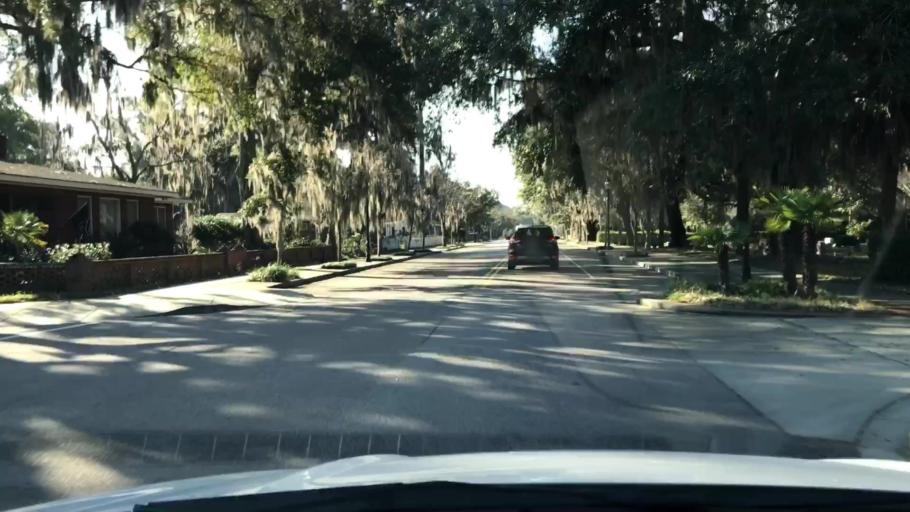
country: US
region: South Carolina
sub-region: Beaufort County
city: Beaufort
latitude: 32.4389
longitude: -80.6795
